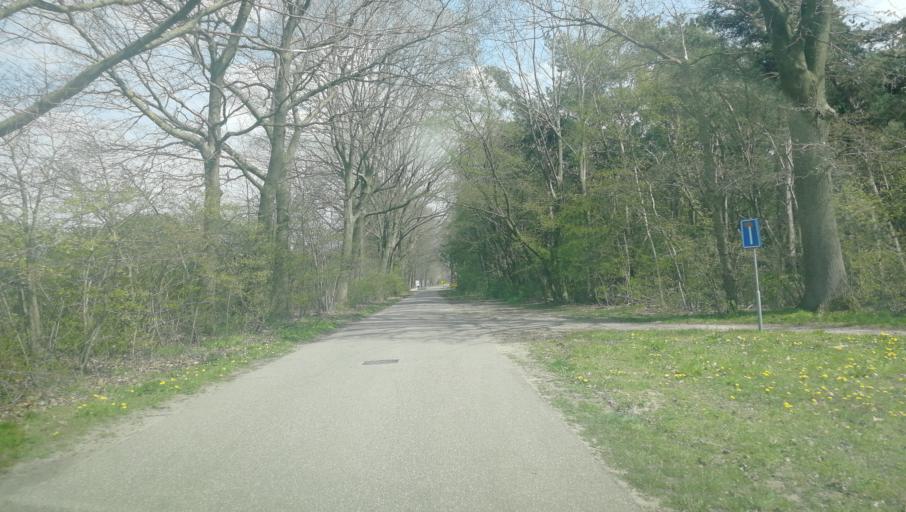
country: NL
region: Limburg
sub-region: Gemeente Venlo
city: Tegelen
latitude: 51.4079
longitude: 6.1097
